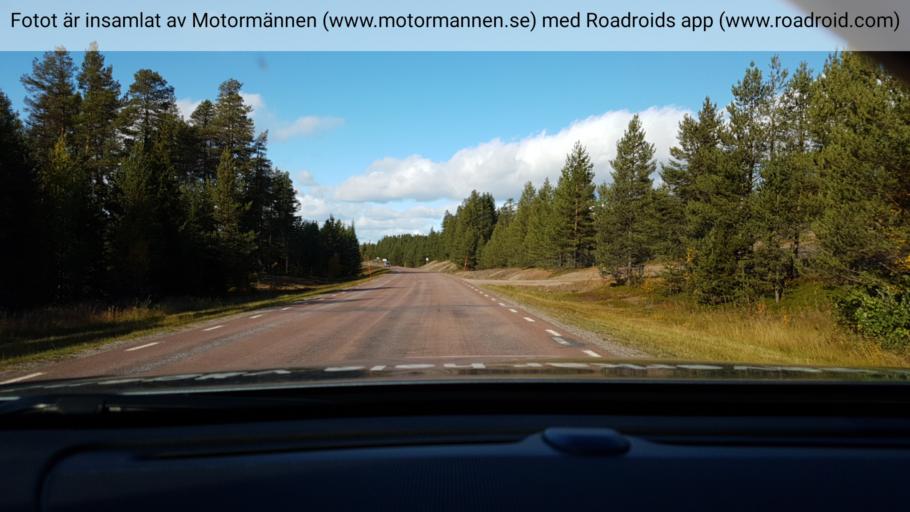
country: SE
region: Norrbotten
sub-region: Arjeplogs Kommun
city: Arjeplog
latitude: 66.0473
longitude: 18.0305
